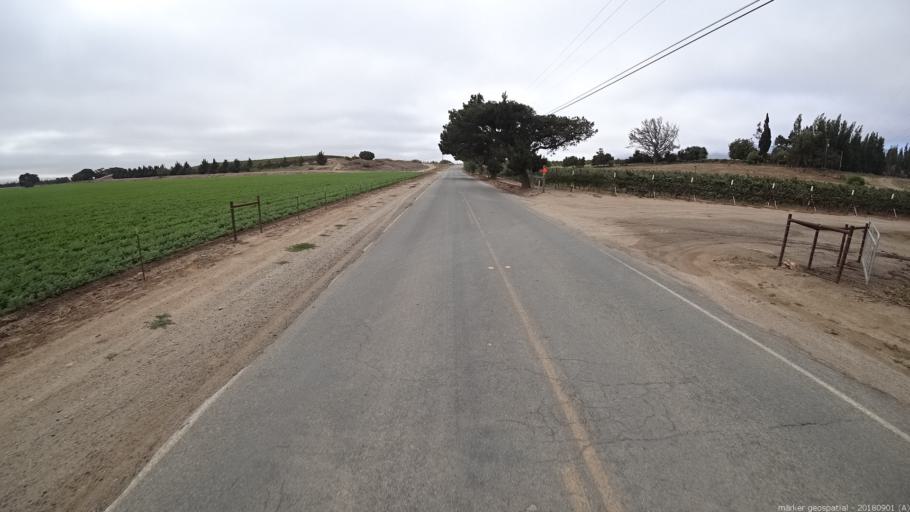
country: US
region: California
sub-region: Monterey County
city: Soledad
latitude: 36.3740
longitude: -121.3262
